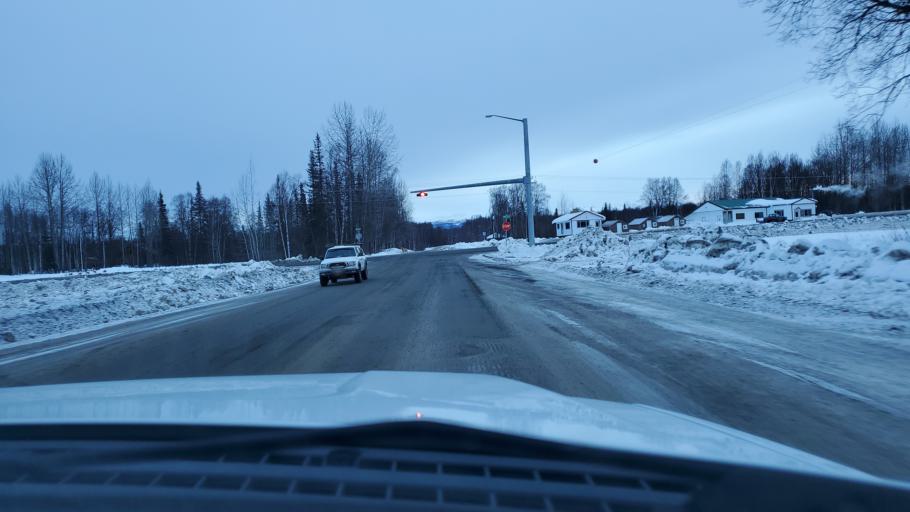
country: US
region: Alaska
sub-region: Matanuska-Susitna Borough
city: Y
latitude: 62.3162
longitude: -150.2352
